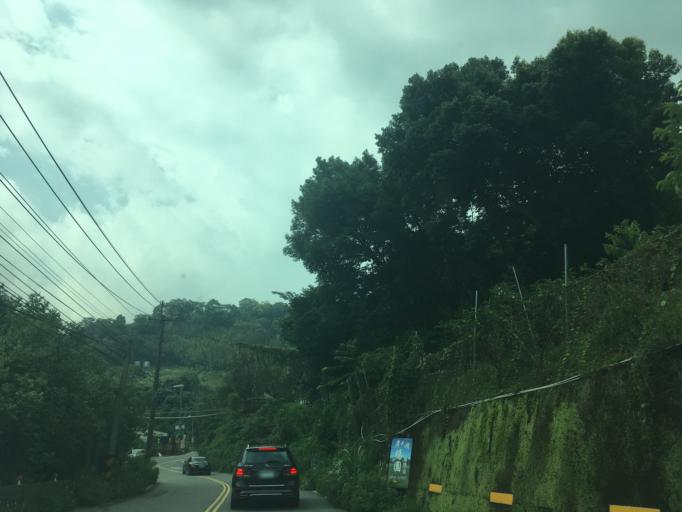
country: TW
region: Taiwan
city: Fengyuan
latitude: 24.3179
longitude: 120.9239
